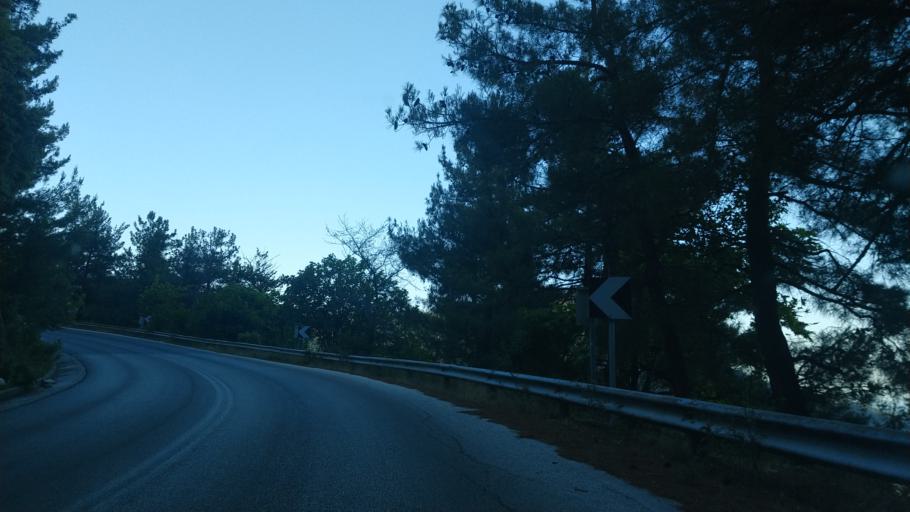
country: GR
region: East Macedonia and Thrace
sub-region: Nomos Kavalas
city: Potamia
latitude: 40.7261
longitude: 24.7332
